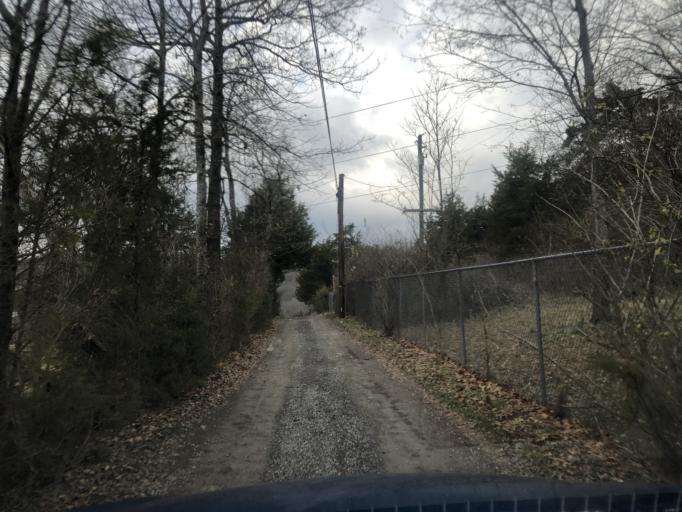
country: US
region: Tennessee
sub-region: Davidson County
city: Belle Meade
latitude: 36.1124
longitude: -86.9301
